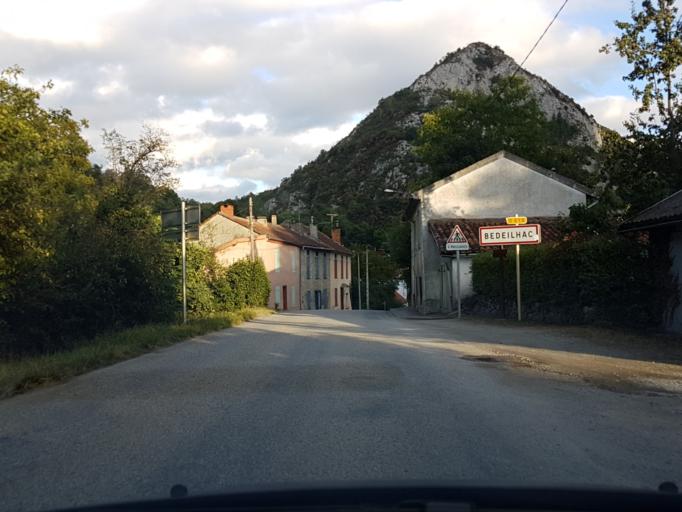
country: FR
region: Midi-Pyrenees
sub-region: Departement de l'Ariege
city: Tarascon-sur-Ariege
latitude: 42.8737
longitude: 1.5628
